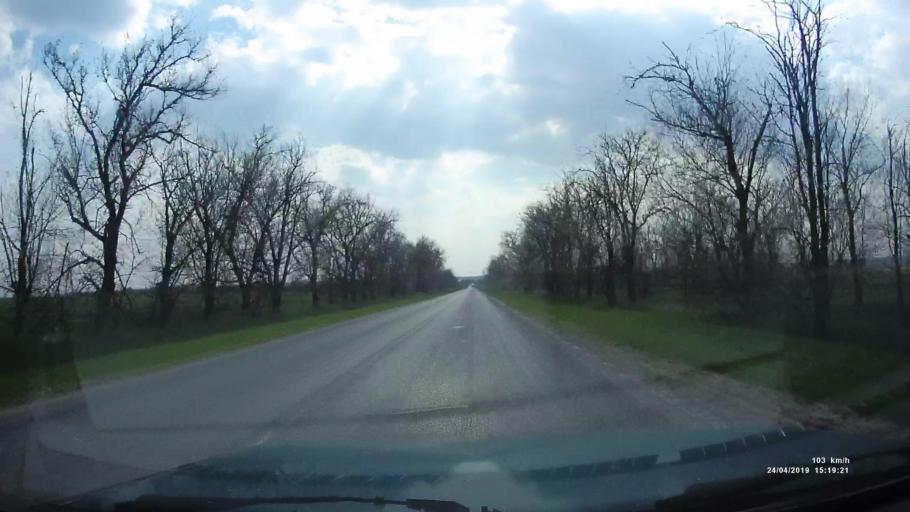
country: RU
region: Rostov
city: Remontnoye
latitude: 46.5406
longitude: 43.1480
